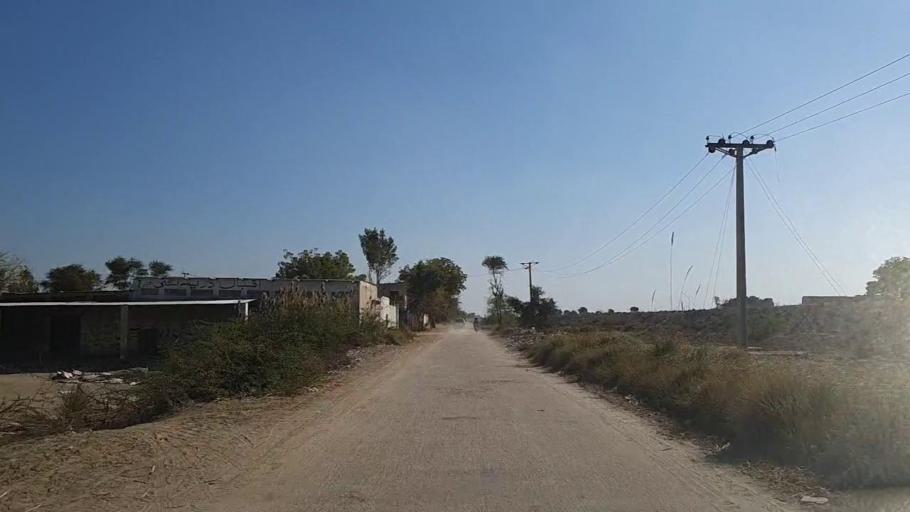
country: PK
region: Sindh
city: Nawabshah
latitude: 26.2395
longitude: 68.4242
